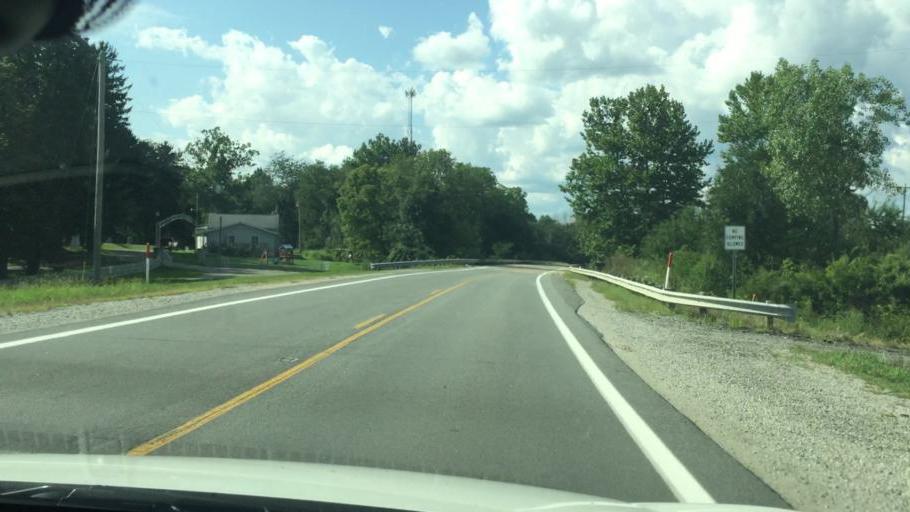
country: US
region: Ohio
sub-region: Madison County
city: Choctaw Lake
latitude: 39.9449
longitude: -83.5016
